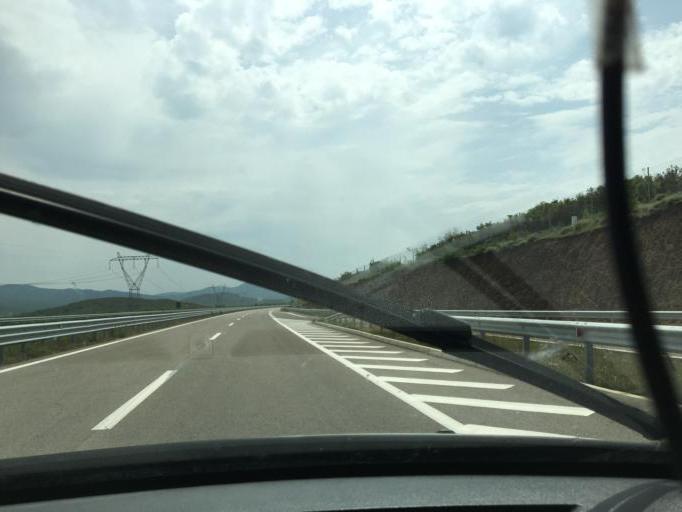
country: MK
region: Gevgelija
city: Miravci
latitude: 41.2789
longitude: 22.4568
